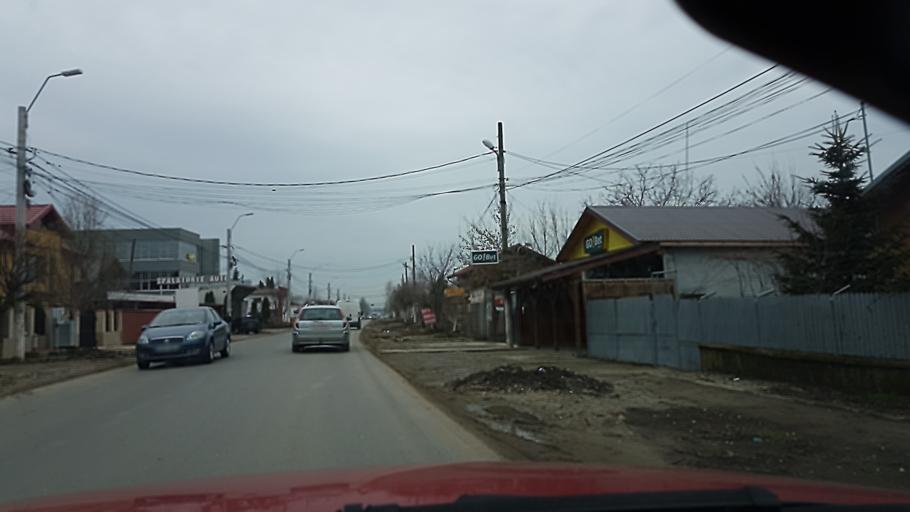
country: RO
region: Ilfov
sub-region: Comuna Tunari
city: Tunari
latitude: 44.5441
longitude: 26.1422
